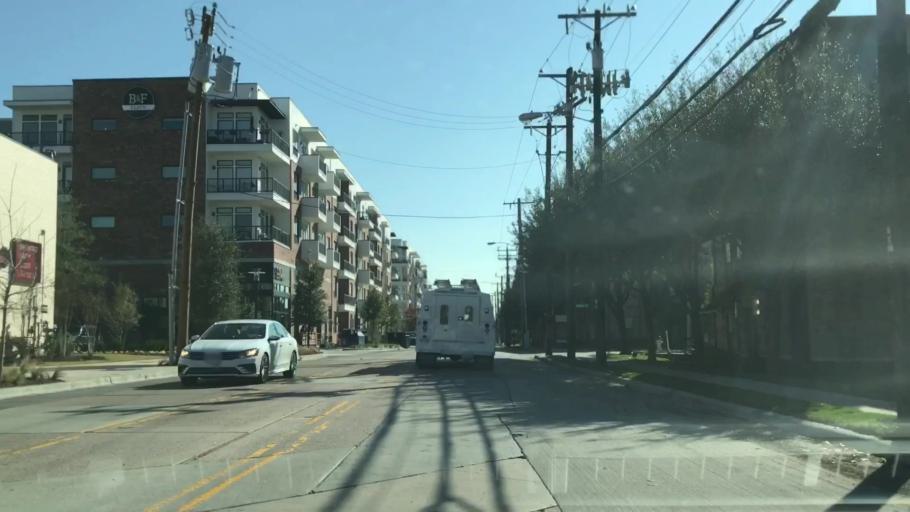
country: US
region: Texas
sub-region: Dallas County
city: Highland Park
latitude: 32.8148
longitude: -96.7862
